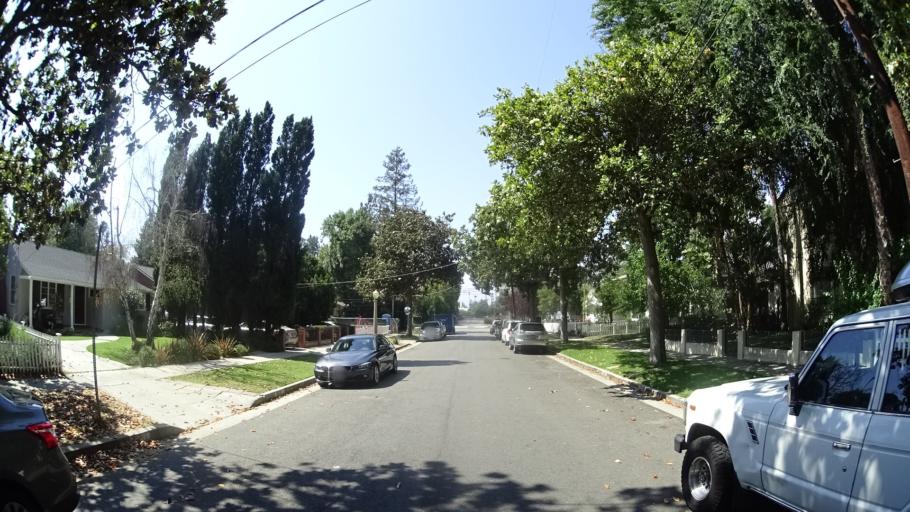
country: US
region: California
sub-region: Los Angeles County
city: North Hollywood
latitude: 34.1401
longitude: -118.3952
